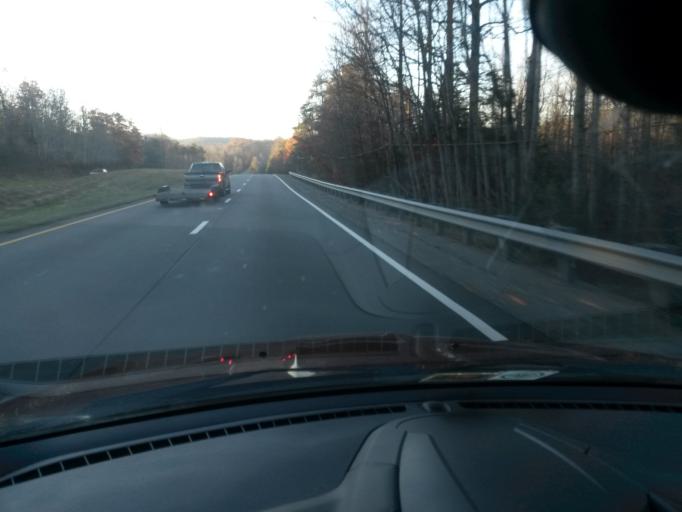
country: US
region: Virginia
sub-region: Franklin County
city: Henry Fork
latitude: 36.9207
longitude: -79.8654
